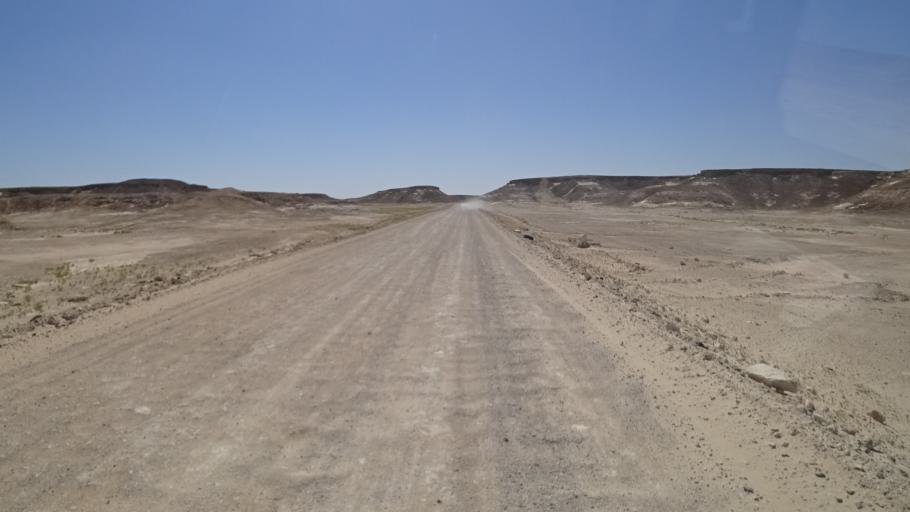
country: OM
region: Zufar
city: Salalah
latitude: 17.4720
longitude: 53.3463
